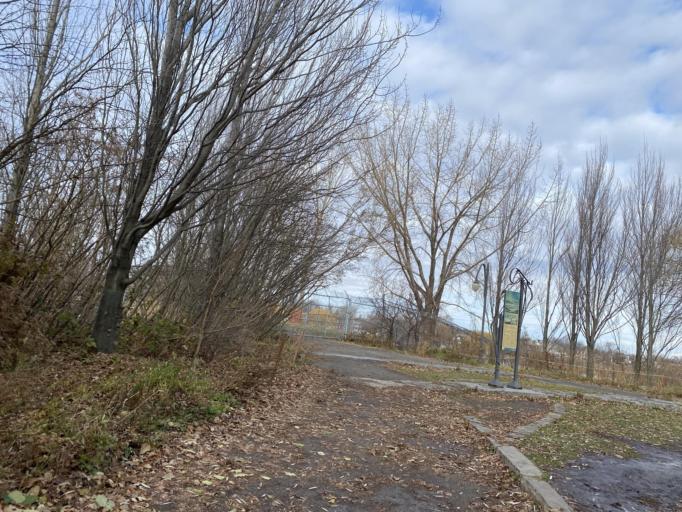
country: CA
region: Quebec
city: Saint-Raymond
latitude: 45.4263
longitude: -73.5916
